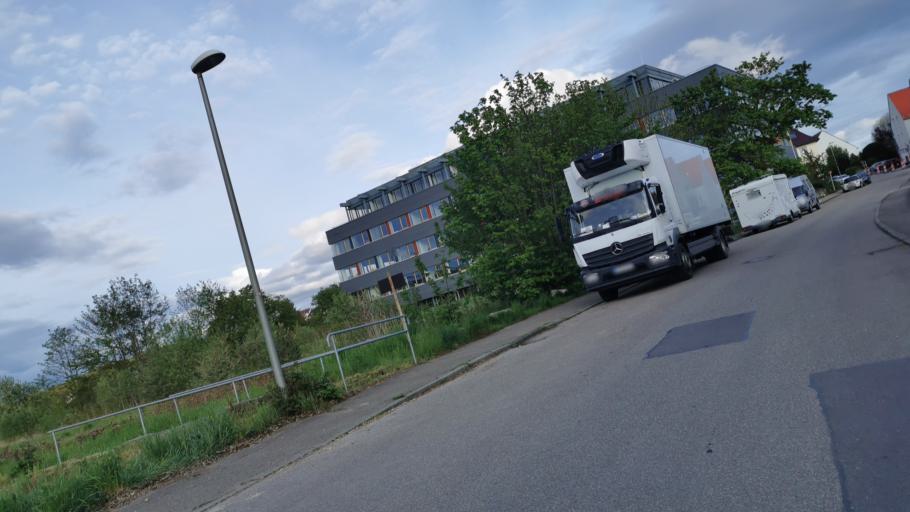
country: DE
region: Baden-Wuerttemberg
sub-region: Regierungsbezirk Stuttgart
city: Korntal
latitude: 48.8206
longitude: 9.1072
